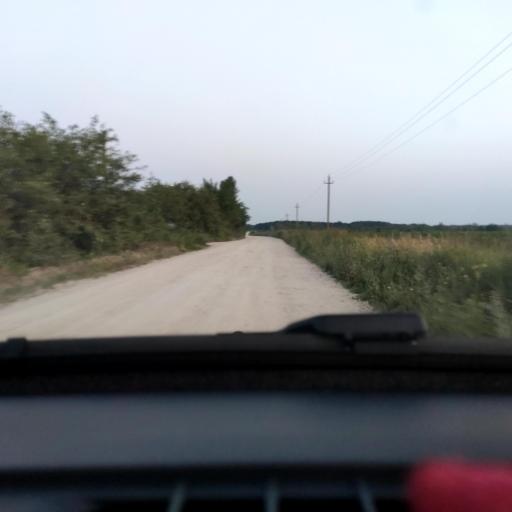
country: RU
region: Voronezj
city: Podgornoye
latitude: 51.8625
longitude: 39.1027
